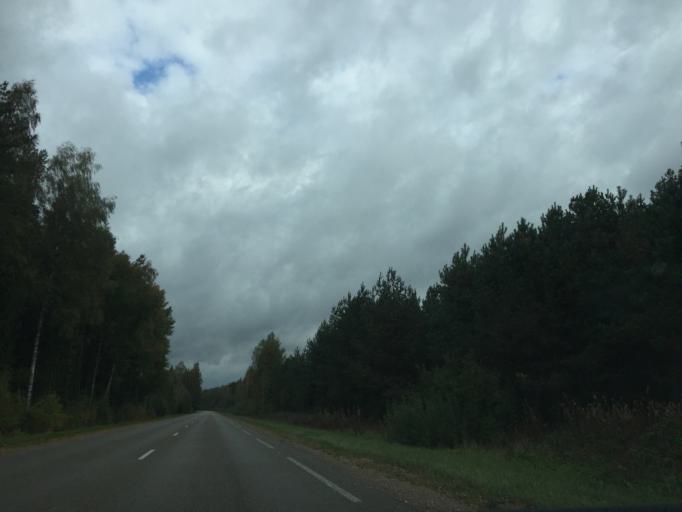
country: LV
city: Tireli
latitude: 56.8260
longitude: 23.6071
